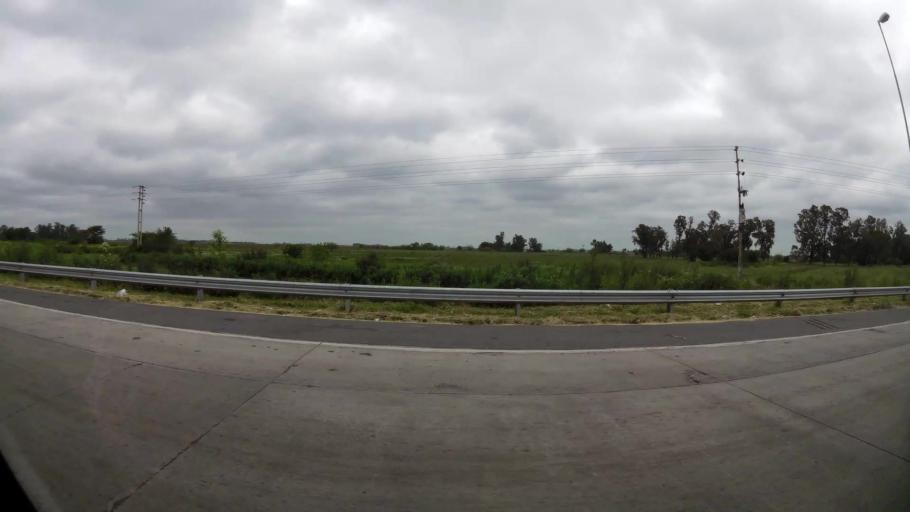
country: AR
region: Buenos Aires
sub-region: Partido de San Vicente
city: San Vicente
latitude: -35.0548
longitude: -58.4426
